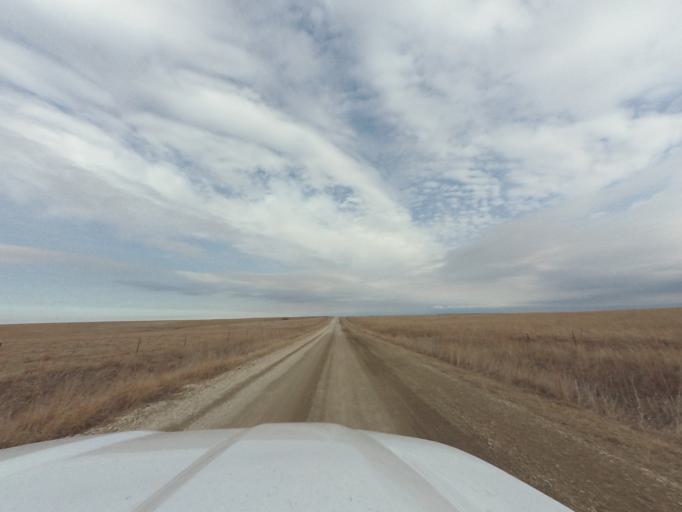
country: US
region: Kansas
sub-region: Chase County
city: Cottonwood Falls
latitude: 38.2393
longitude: -96.7305
